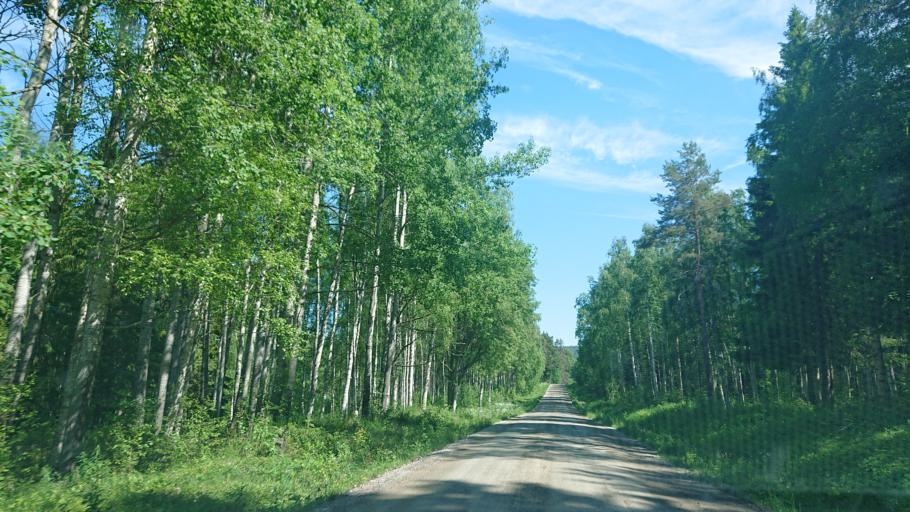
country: SE
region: Vaesternorrland
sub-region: Solleftea Kommun
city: Solleftea
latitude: 62.9707
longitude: 17.1604
